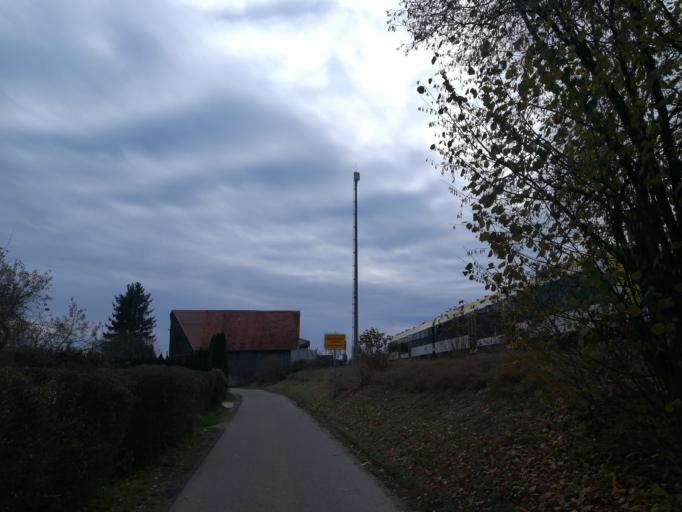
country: DE
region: Baden-Wuerttemberg
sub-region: Regierungsbezirk Stuttgart
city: Sontheim an der Brenz
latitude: 48.5628
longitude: 10.2844
